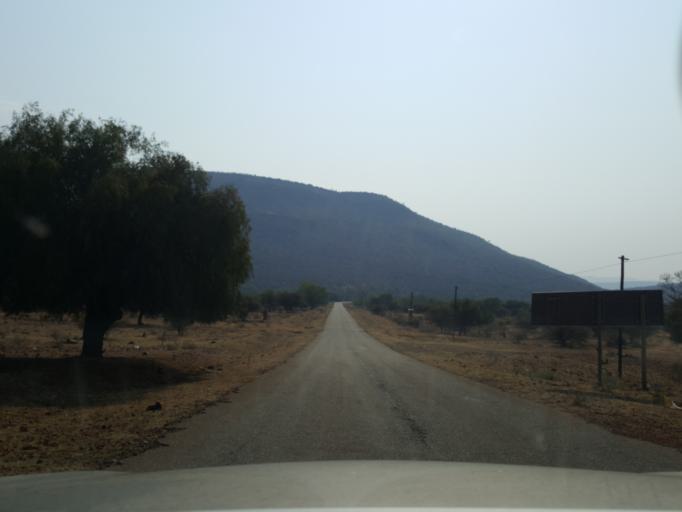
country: BW
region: South East
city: Lobatse
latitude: -25.3292
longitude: 25.7664
